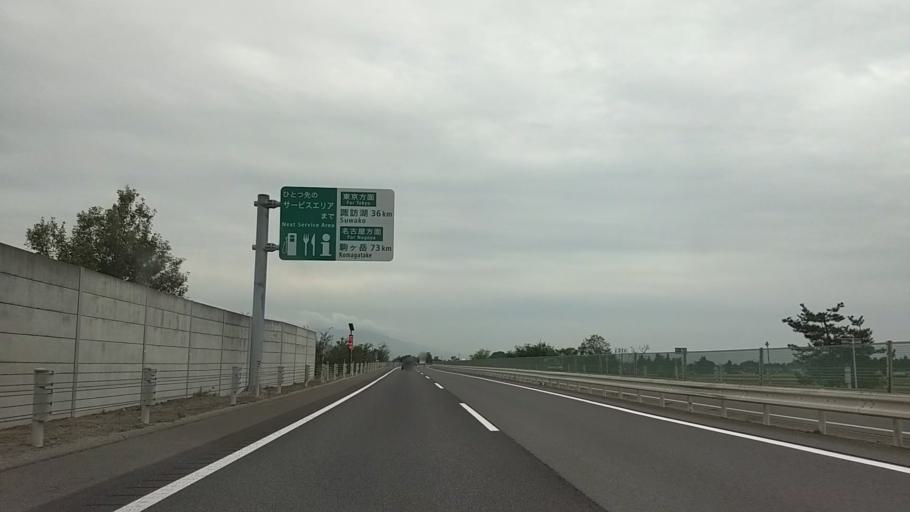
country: JP
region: Nagano
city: Toyoshina
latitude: 36.2862
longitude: 137.9292
